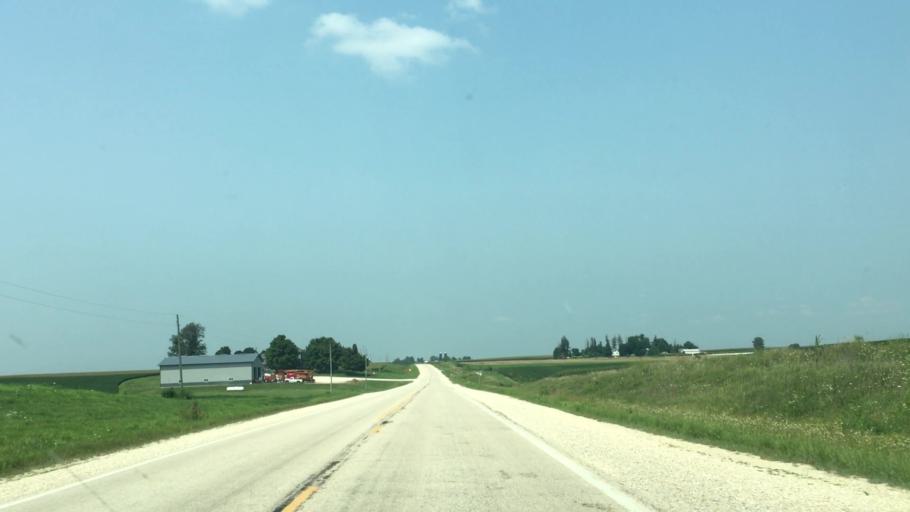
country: US
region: Iowa
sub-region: Fayette County
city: West Union
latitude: 42.9891
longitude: -91.8241
